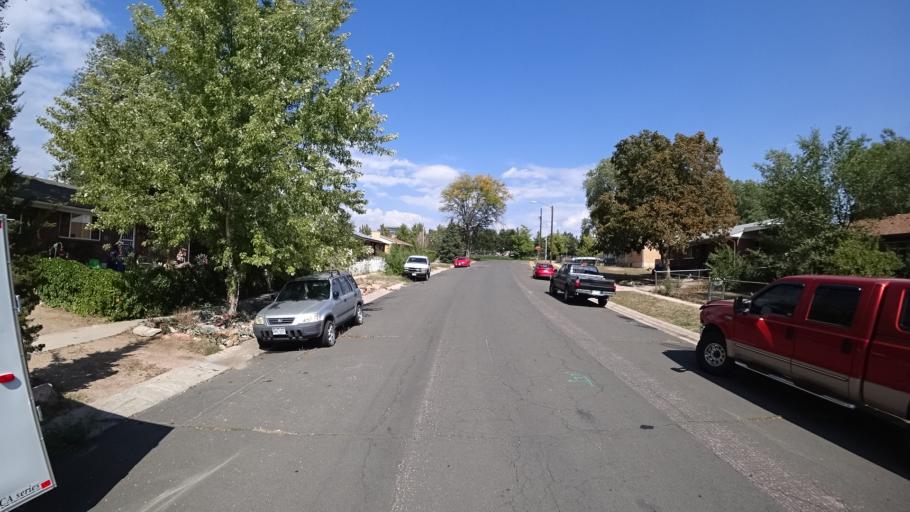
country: US
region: Colorado
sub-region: El Paso County
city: Colorado Springs
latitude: 38.8245
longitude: -104.7870
